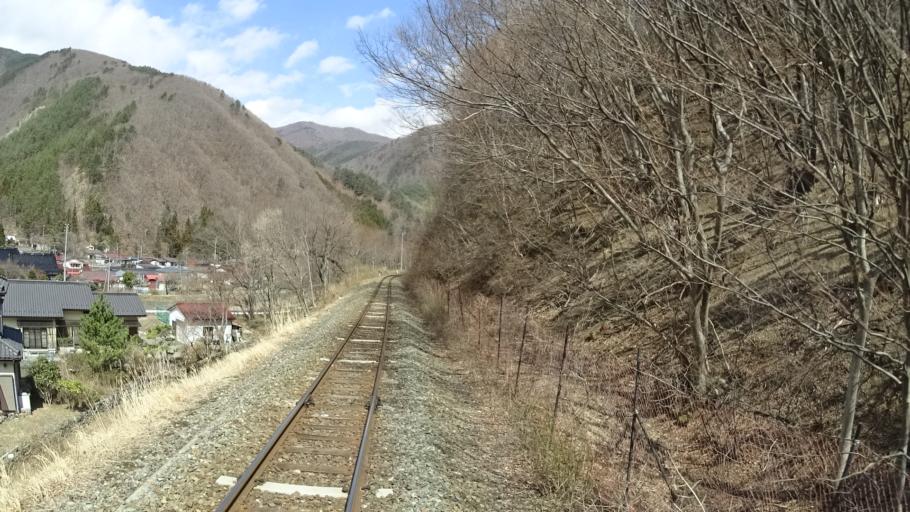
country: JP
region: Iwate
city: Kamaishi
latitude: 39.2524
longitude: 141.7430
